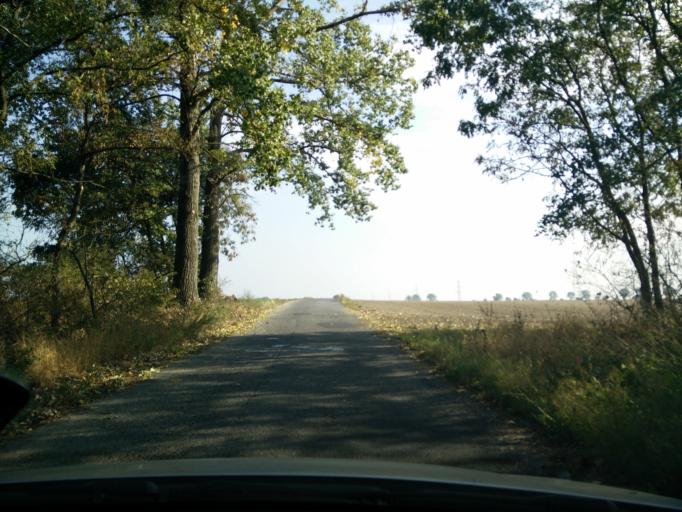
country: PL
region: Greater Poland Voivodeship
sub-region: Powiat sredzki
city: Sroda Wielkopolska
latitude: 52.3022
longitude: 17.2574
